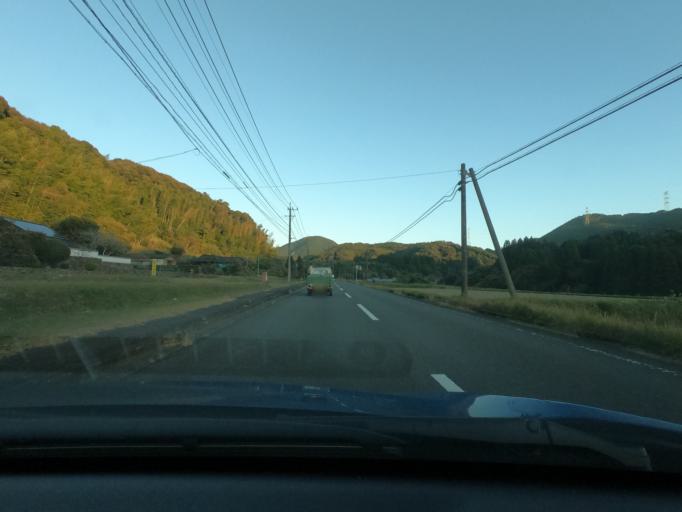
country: JP
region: Kagoshima
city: Satsumasendai
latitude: 31.7903
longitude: 130.4643
